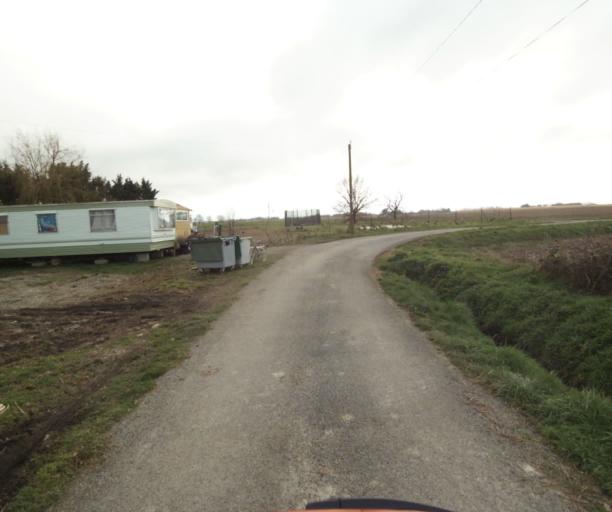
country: FR
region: Midi-Pyrenees
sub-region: Departement de l'Ariege
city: Mazeres
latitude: 43.2008
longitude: 1.6783
